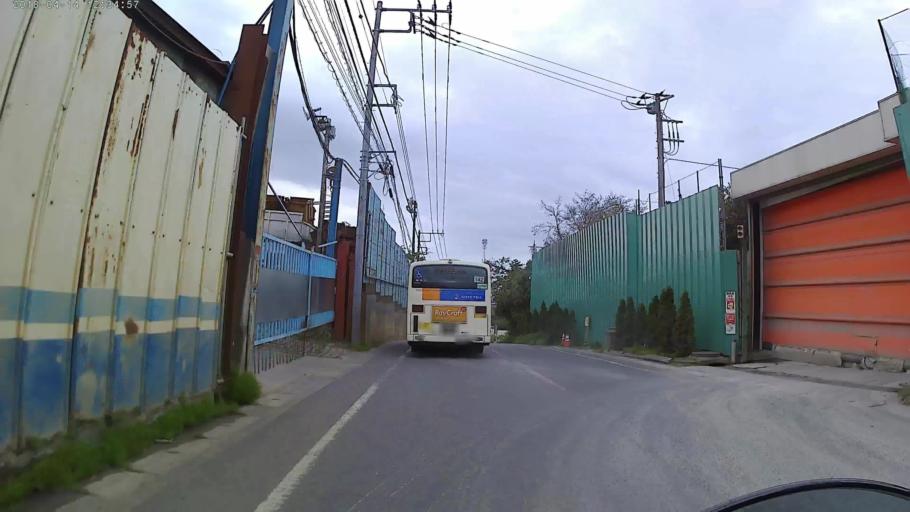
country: JP
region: Kanagawa
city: Atsugi
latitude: 35.4234
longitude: 139.4092
